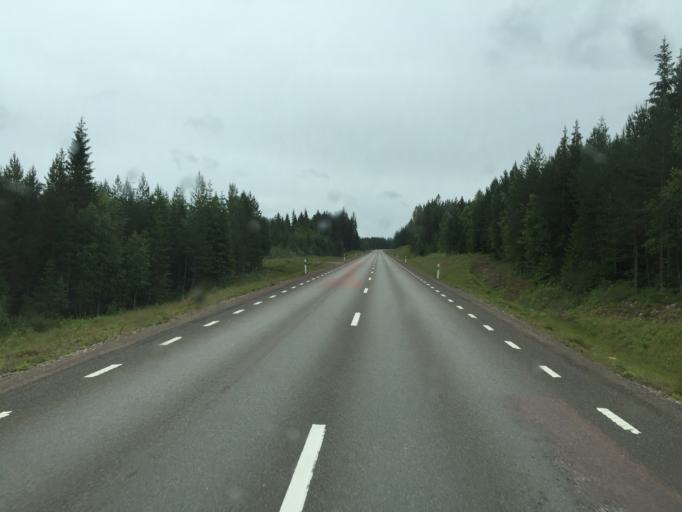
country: SE
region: Dalarna
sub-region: Malung-Saelens kommun
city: Malung
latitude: 60.5920
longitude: 13.5802
